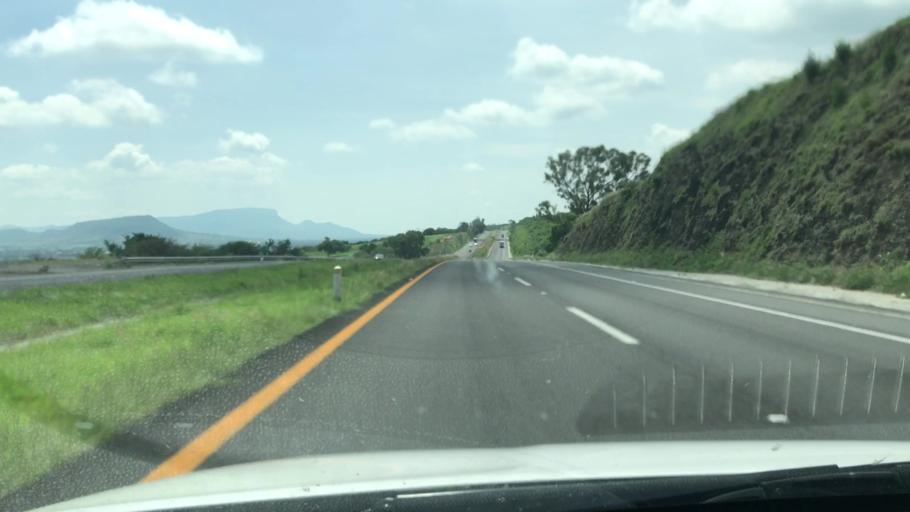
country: MX
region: Jalisco
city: Ocotlan
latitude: 20.4341
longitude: -102.7939
